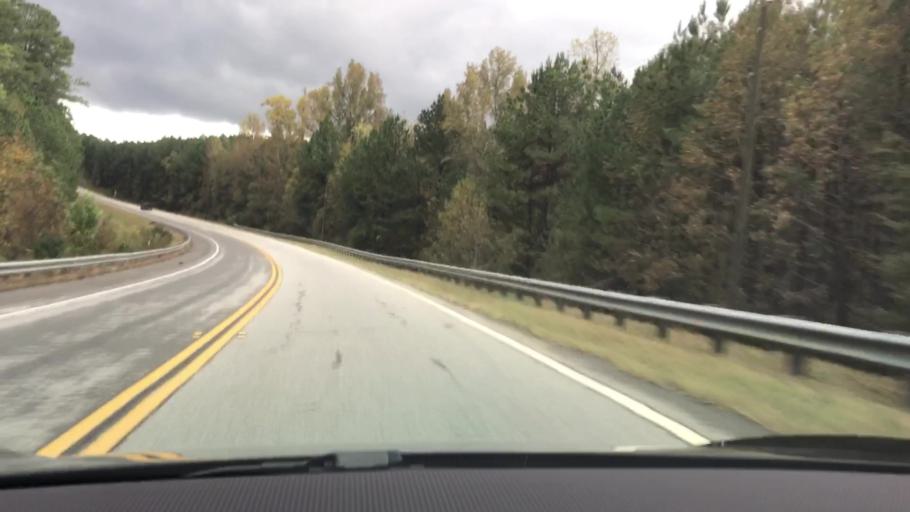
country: US
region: Georgia
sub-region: Greene County
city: Greensboro
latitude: 33.7087
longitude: -83.2912
